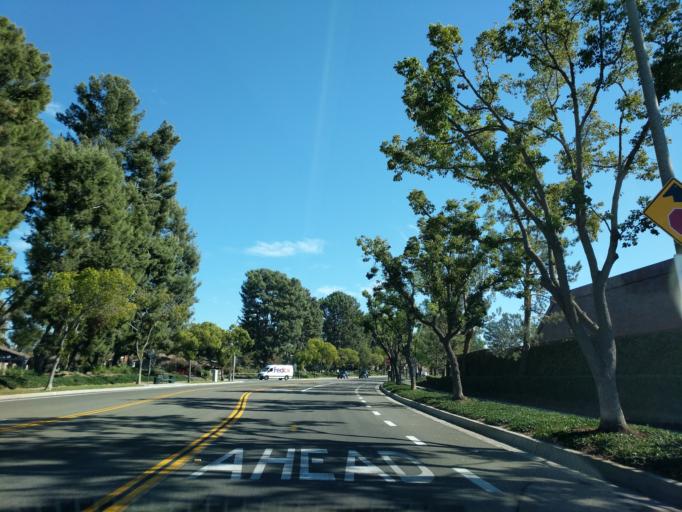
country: US
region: California
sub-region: Orange County
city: Irvine
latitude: 33.6603
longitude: -117.8029
